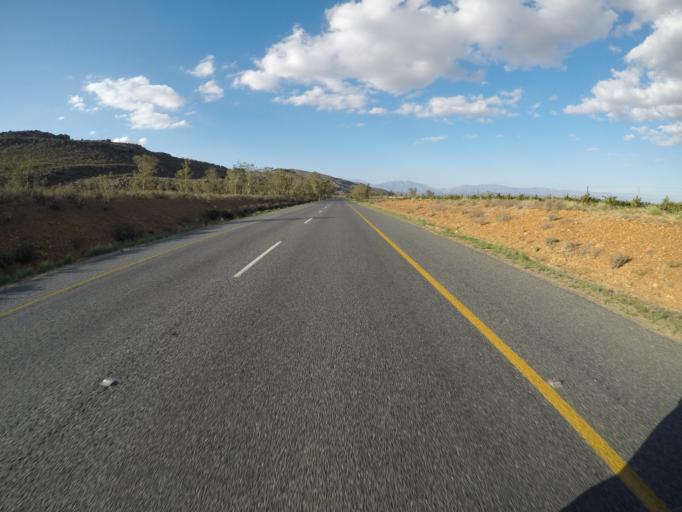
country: ZA
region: Western Cape
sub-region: Cape Winelands District Municipality
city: Worcester
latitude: -33.8004
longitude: 19.4392
